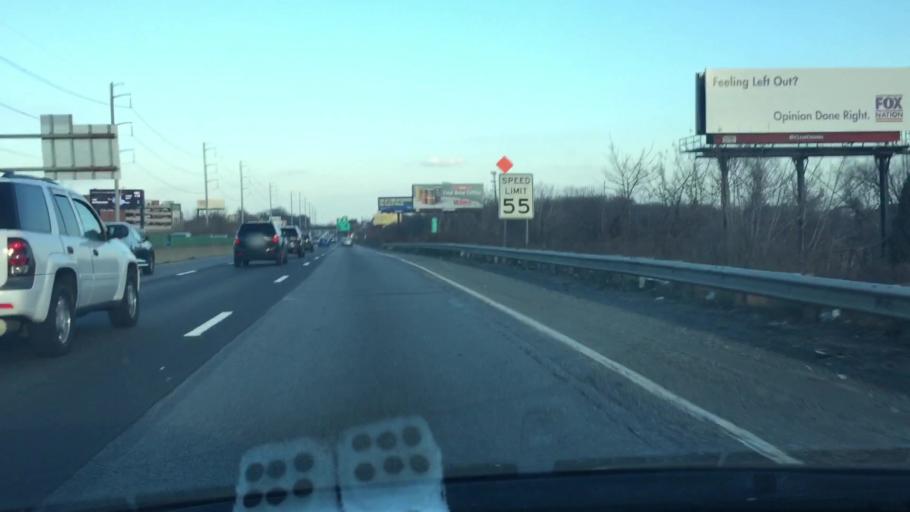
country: US
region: Pennsylvania
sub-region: Delaware County
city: Upland
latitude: 39.8520
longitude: -75.3731
